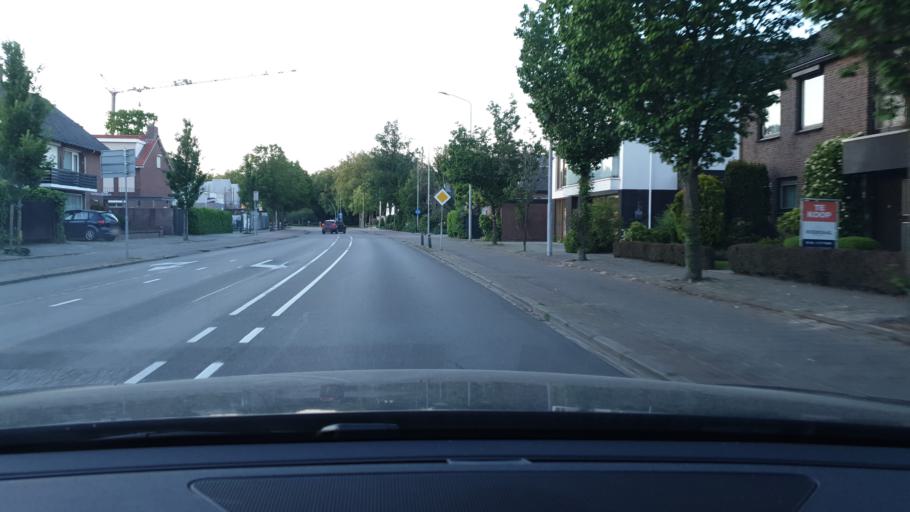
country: NL
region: North Brabant
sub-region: Gemeente Valkenswaard
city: Valkenswaard
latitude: 51.3511
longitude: 5.4516
